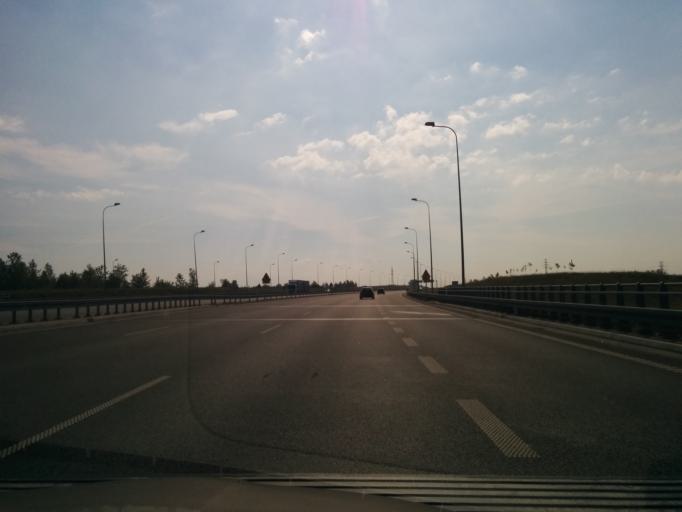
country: PL
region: Silesian Voivodeship
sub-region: Powiat tarnogorski
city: Radzionkow
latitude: 50.3726
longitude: 18.8994
